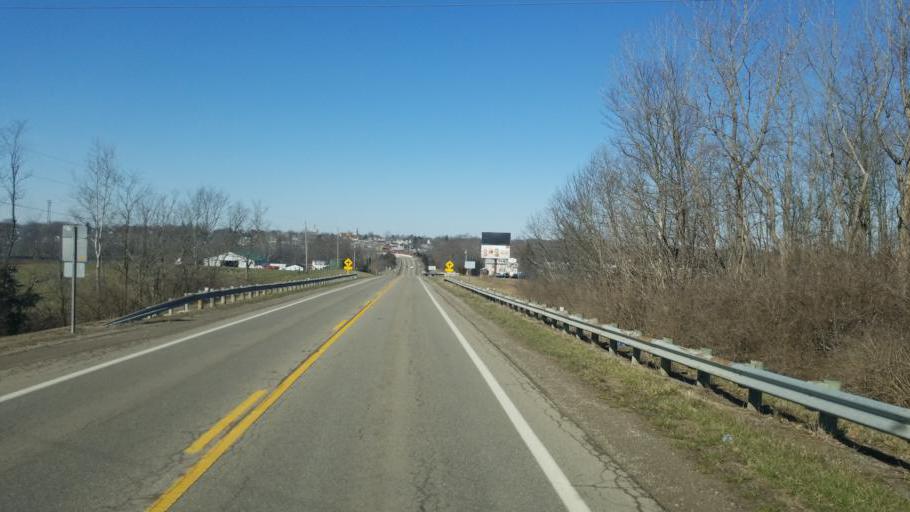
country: US
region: Ohio
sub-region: Highland County
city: Greenfield
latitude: 39.3530
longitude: -83.3688
